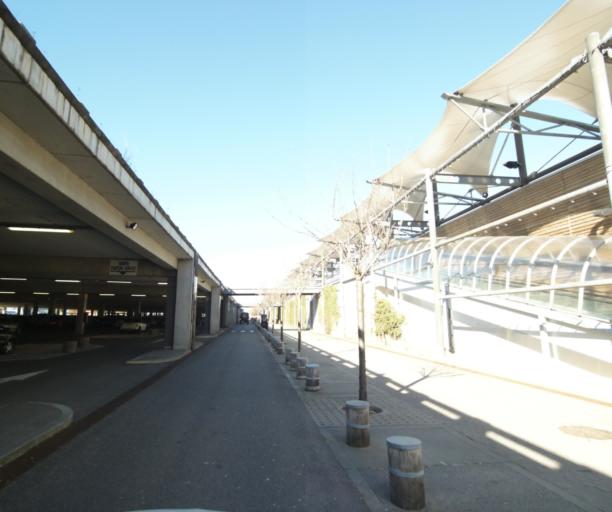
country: FR
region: Lorraine
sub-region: Departement de Meurthe-et-Moselle
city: Vandoeuvre-les-Nancy
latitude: 48.6396
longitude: 6.1849
